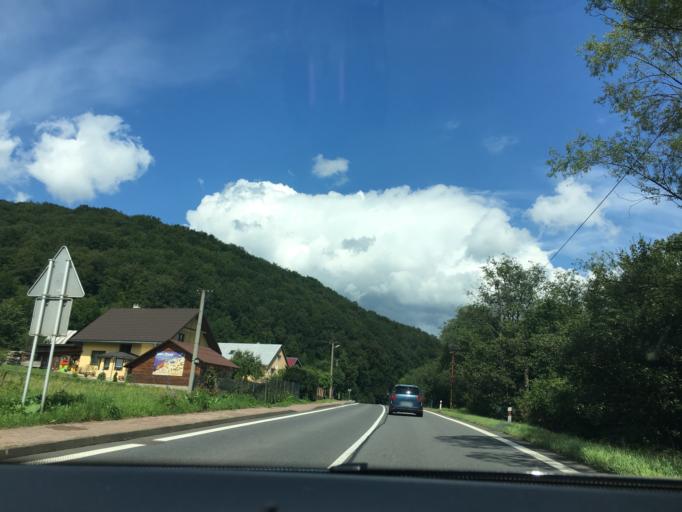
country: SK
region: Presovsky
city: Svidnik
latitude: 49.3637
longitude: 21.6592
